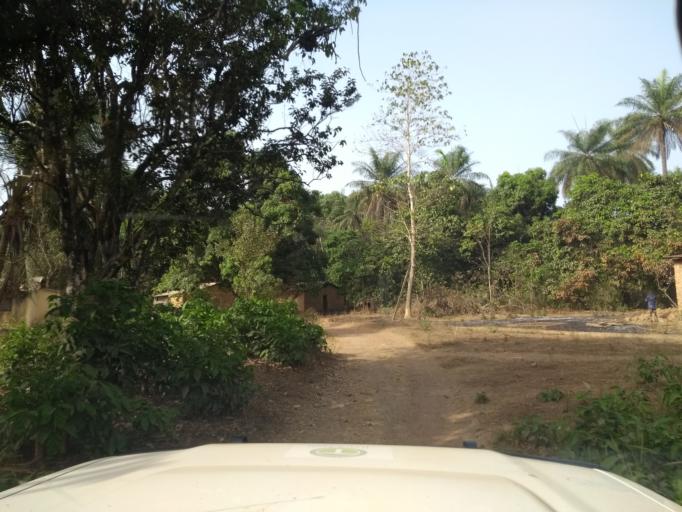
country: GN
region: Kindia
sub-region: Prefecture de Dubreka
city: Dubreka
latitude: 9.8214
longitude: -13.5550
